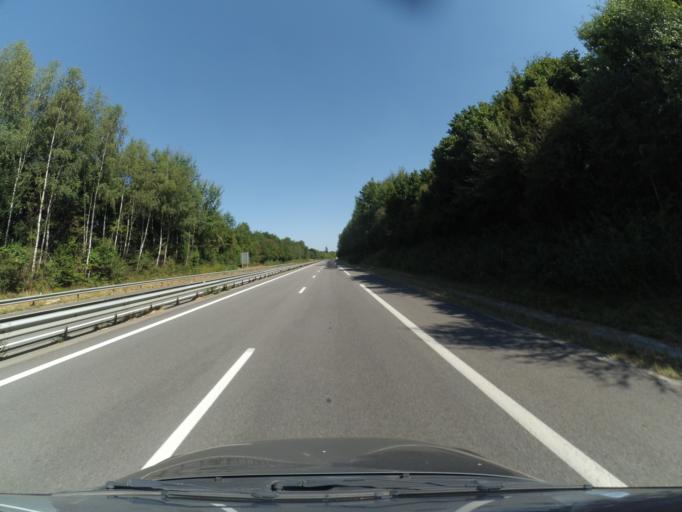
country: FR
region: Limousin
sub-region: Departement de la Haute-Vienne
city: Verneuil-sur-Vienne
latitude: 45.8586
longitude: 1.1463
